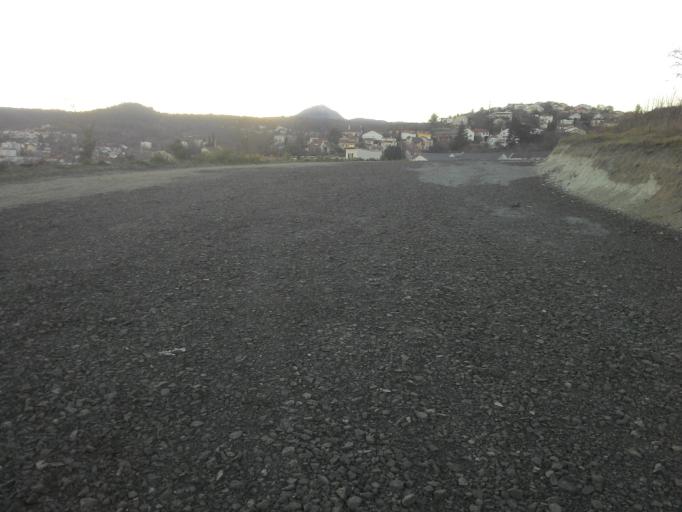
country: FR
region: Auvergne
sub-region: Departement du Puy-de-Dome
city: Durtol
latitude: 45.7939
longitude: 3.0679
